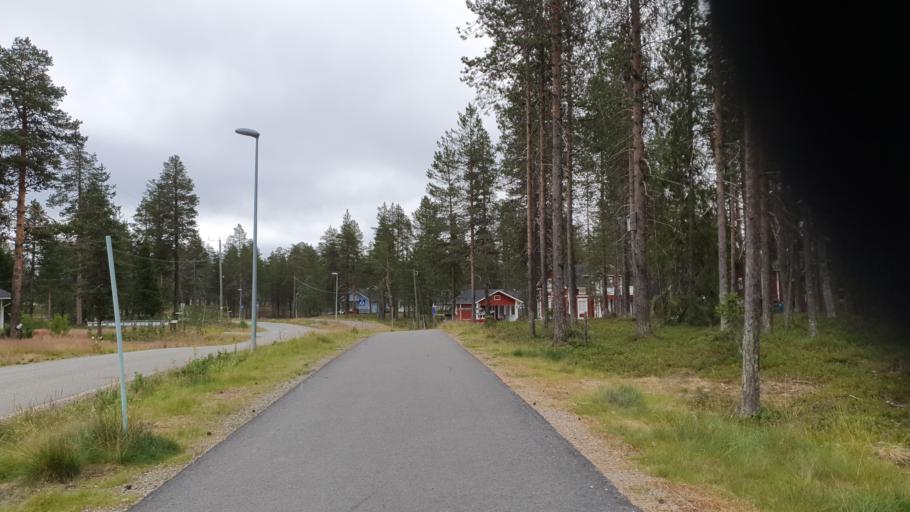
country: FI
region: Lapland
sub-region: Tunturi-Lappi
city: Kolari
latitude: 67.6243
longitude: 24.1477
